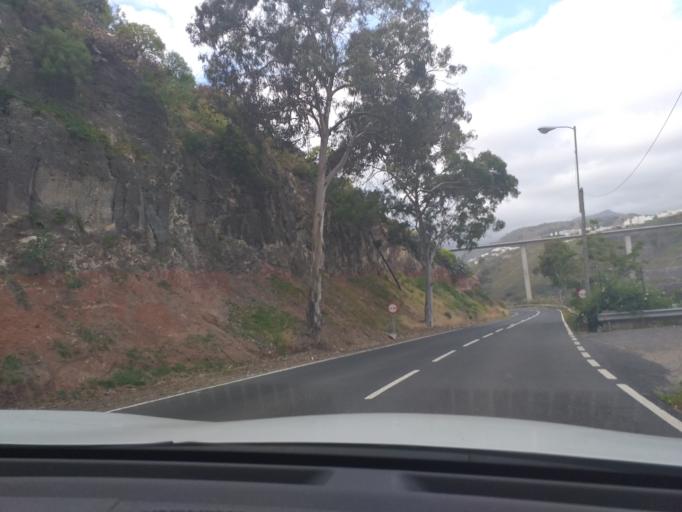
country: ES
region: Canary Islands
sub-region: Provincia de Las Palmas
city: Arucas
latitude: 28.1160
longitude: -15.4940
